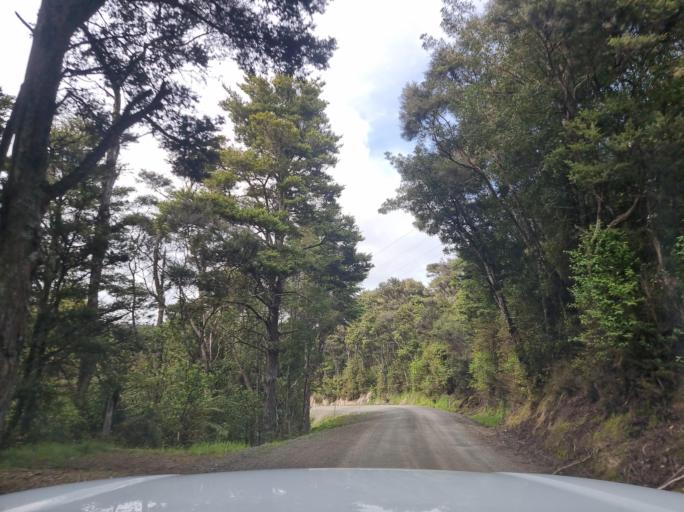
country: NZ
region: Northland
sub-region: Whangarei
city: Ruakaka
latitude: -36.1046
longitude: 174.2062
